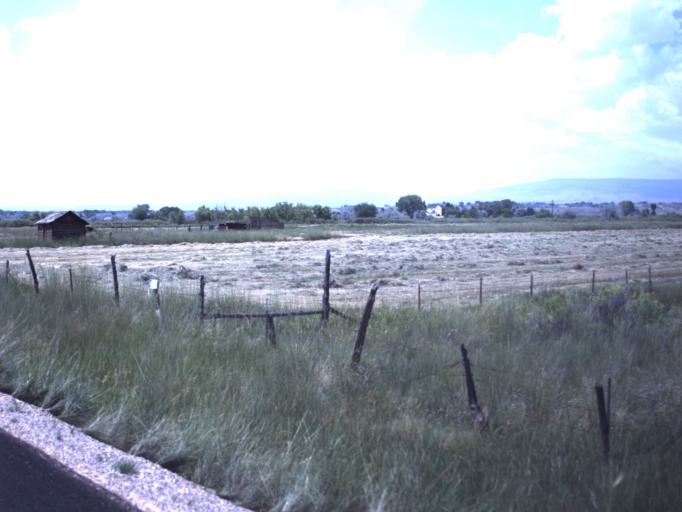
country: US
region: Utah
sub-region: Duchesne County
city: Roosevelt
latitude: 40.4037
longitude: -109.8453
